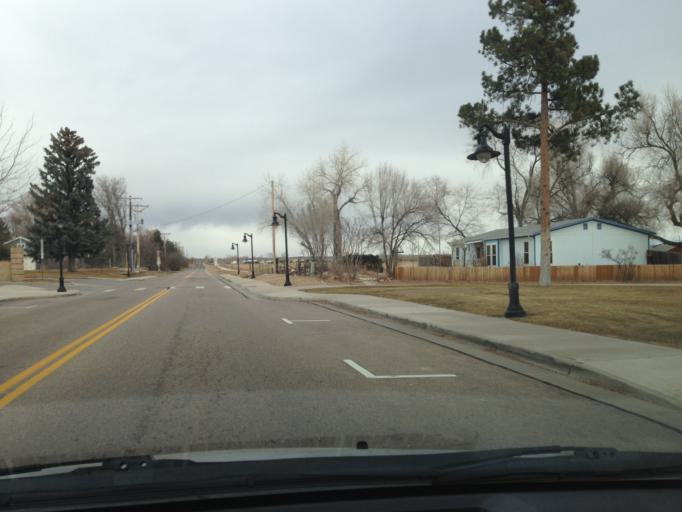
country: US
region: Colorado
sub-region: Weld County
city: Windsor
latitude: 40.5326
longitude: -104.9823
